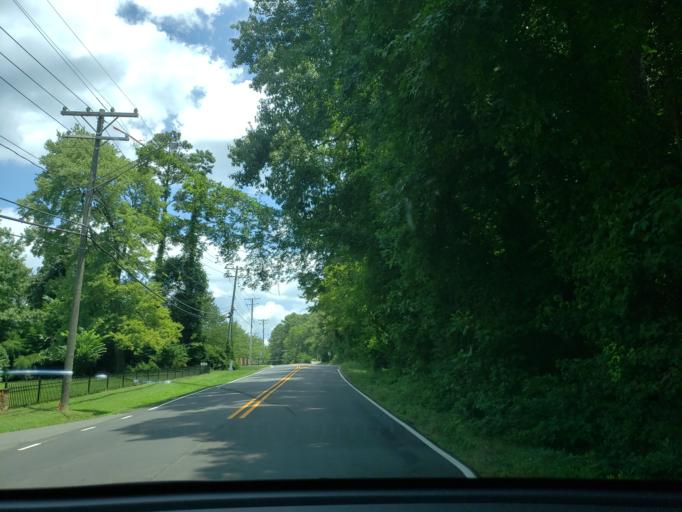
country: US
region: North Carolina
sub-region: Durham County
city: Durham
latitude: 35.9532
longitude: -78.9580
